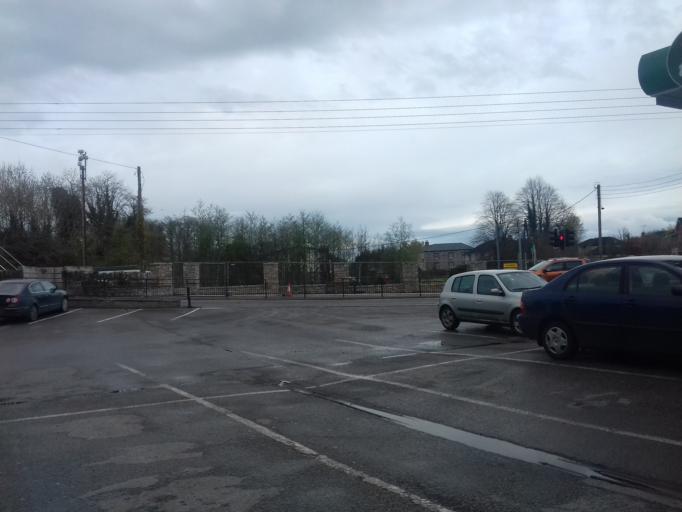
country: IE
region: Ulster
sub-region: An Cabhan
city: Ballyconnell
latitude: 54.1154
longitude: -7.5832
